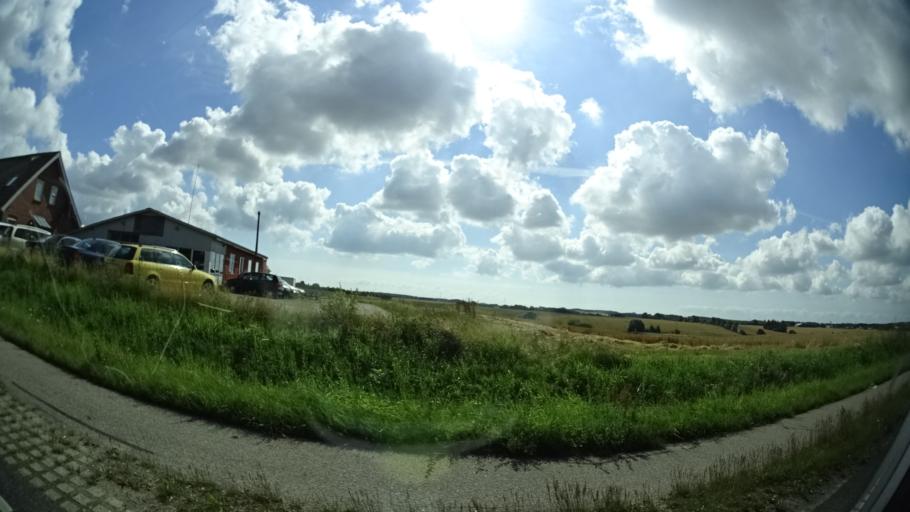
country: DK
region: Central Jutland
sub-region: Odder Kommune
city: Odder
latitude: 55.9995
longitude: 10.1660
